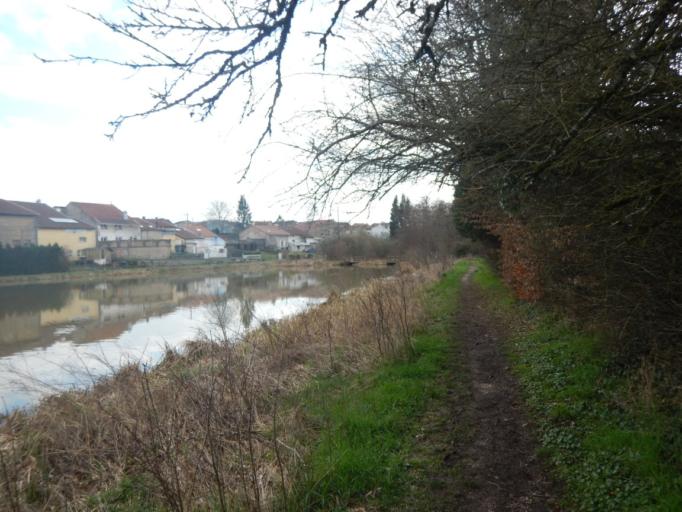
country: FR
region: Lorraine
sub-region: Departement de la Moselle
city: Lorquin
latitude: 48.6858
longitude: 6.9245
